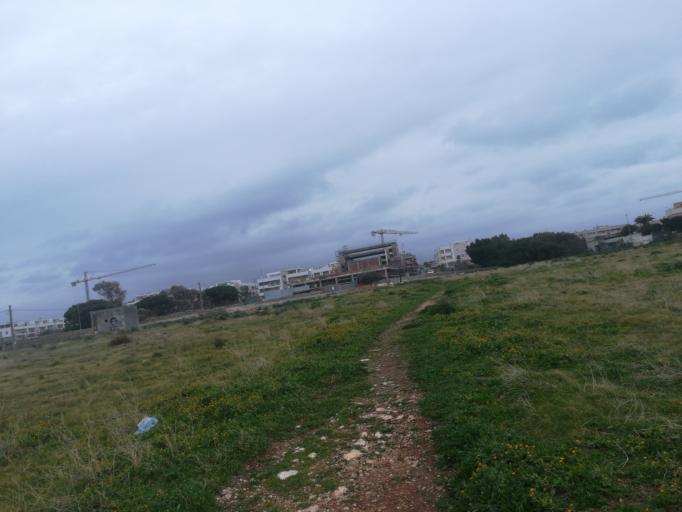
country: IT
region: Apulia
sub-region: Provincia di Bari
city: Polignano a Mare
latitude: 40.9910
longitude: 17.2339
